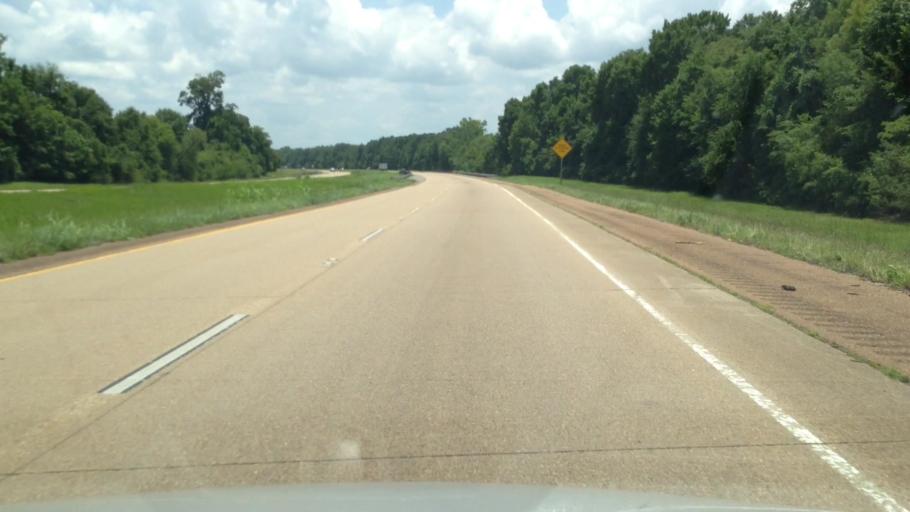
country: US
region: Louisiana
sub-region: Rapides Parish
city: Woodworth
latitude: 31.1457
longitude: -92.4528
